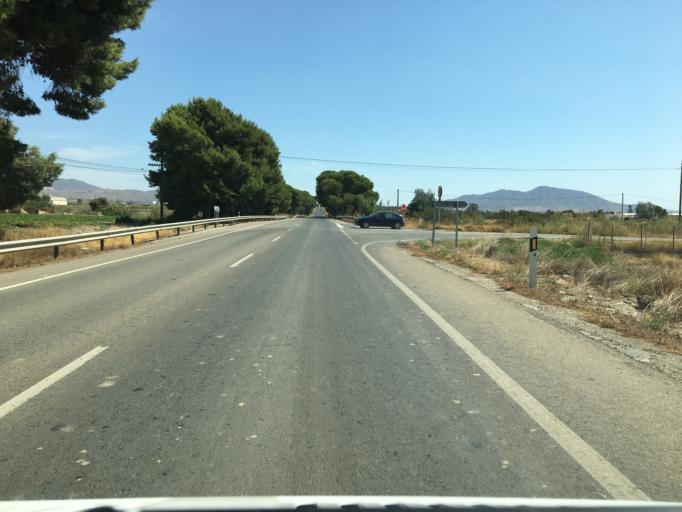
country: ES
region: Andalusia
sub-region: Provincia de Almeria
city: Huercal-Overa
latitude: 37.4217
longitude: -1.9202
